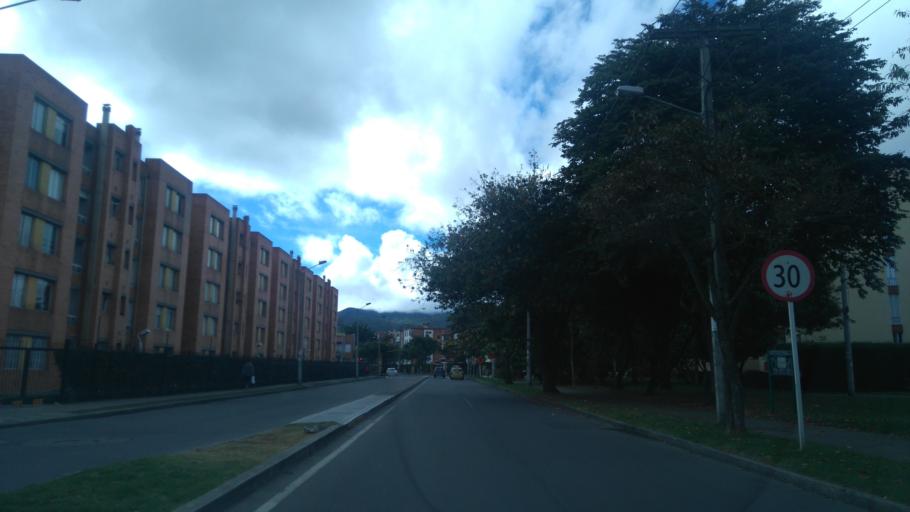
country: CO
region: Cundinamarca
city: Cota
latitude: 4.7661
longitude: -74.0486
